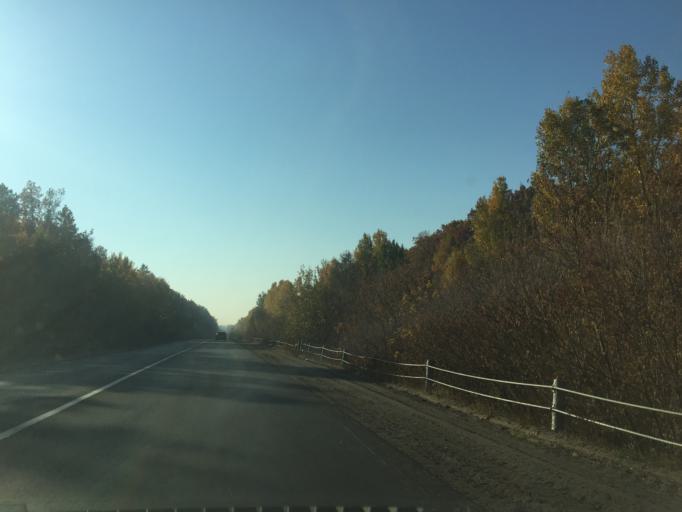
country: BY
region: Gomel
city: Gomel
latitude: 52.4162
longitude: 30.8286
